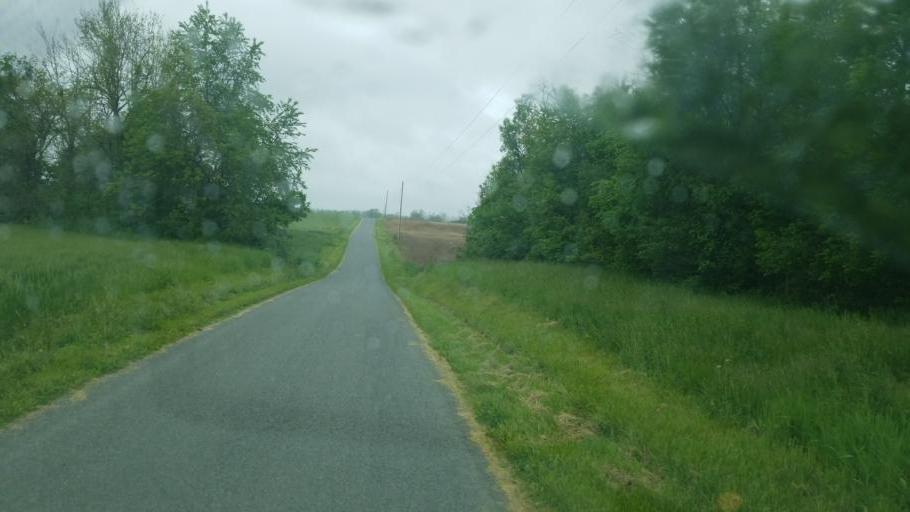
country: US
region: Ohio
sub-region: Highland County
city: Greenfield
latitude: 39.3316
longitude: -83.4554
